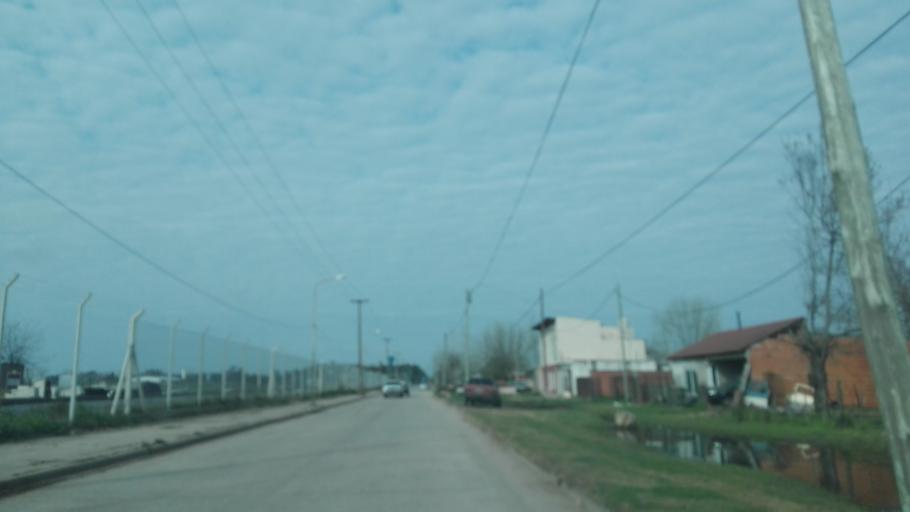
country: AR
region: Buenos Aires
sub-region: Partido de Chascomus
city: Chascomus
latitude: -35.5742
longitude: -57.9844
